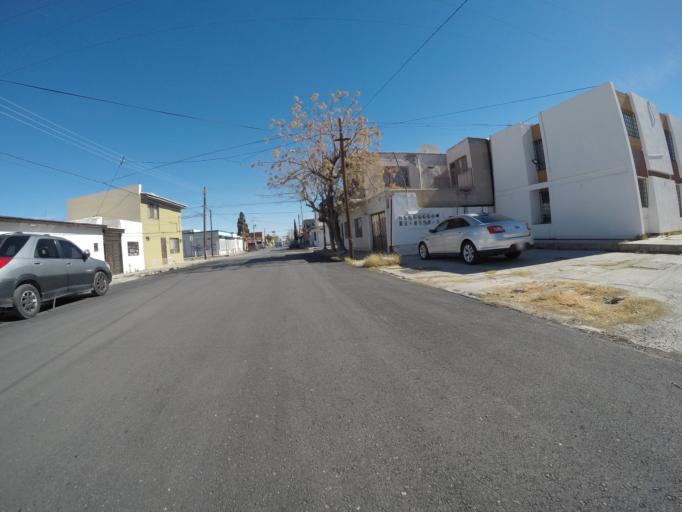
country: MX
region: Chihuahua
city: Ciudad Juarez
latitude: 31.7407
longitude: -106.4676
